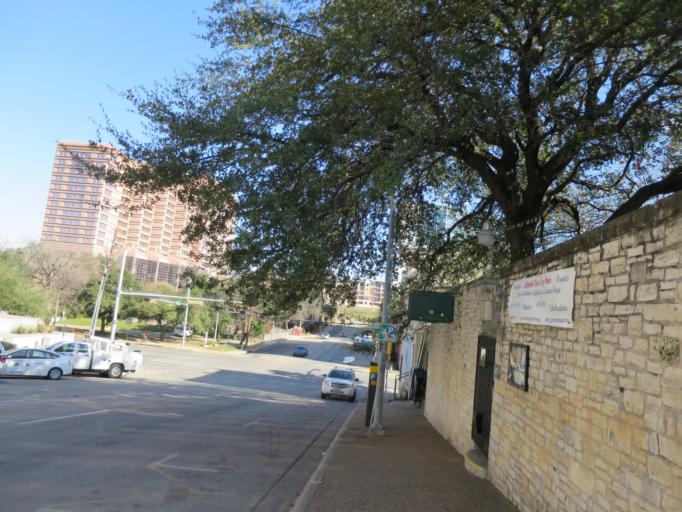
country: US
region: Texas
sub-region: Travis County
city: Austin
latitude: 30.2707
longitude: -97.7363
